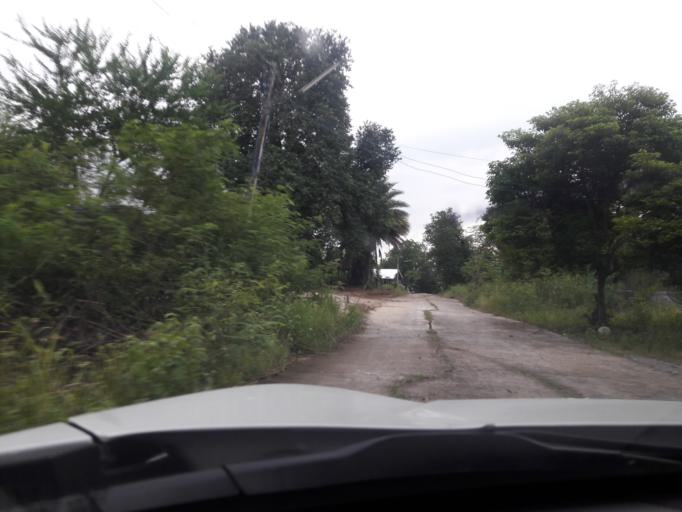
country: TH
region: Lop Buri
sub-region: Amphoe Tha Luang
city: Tha Luang
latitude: 15.0677
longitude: 101.1114
